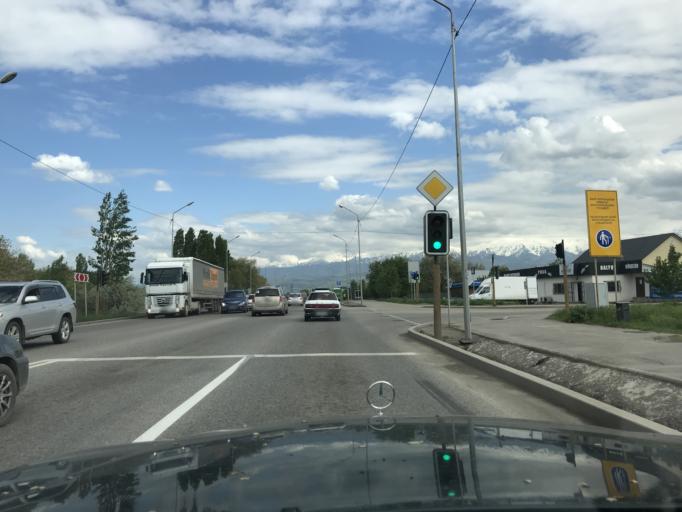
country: KZ
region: Almaty Oblysy
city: Burunday
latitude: 43.3082
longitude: 76.8750
